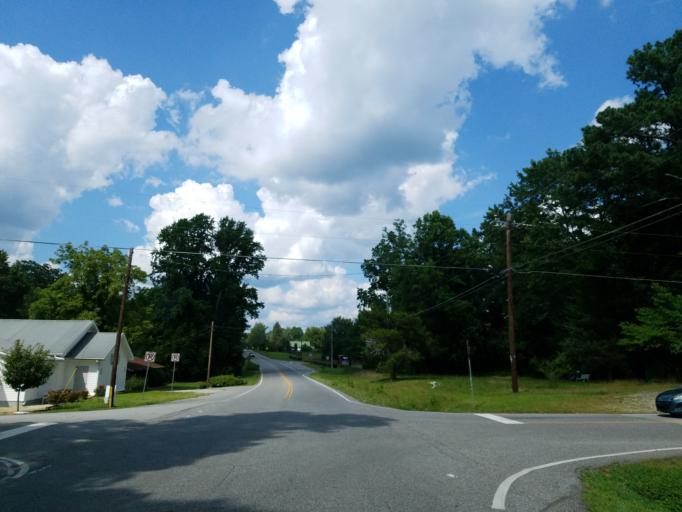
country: US
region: Georgia
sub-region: Dawson County
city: Dawsonville
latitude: 34.4250
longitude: -84.1063
